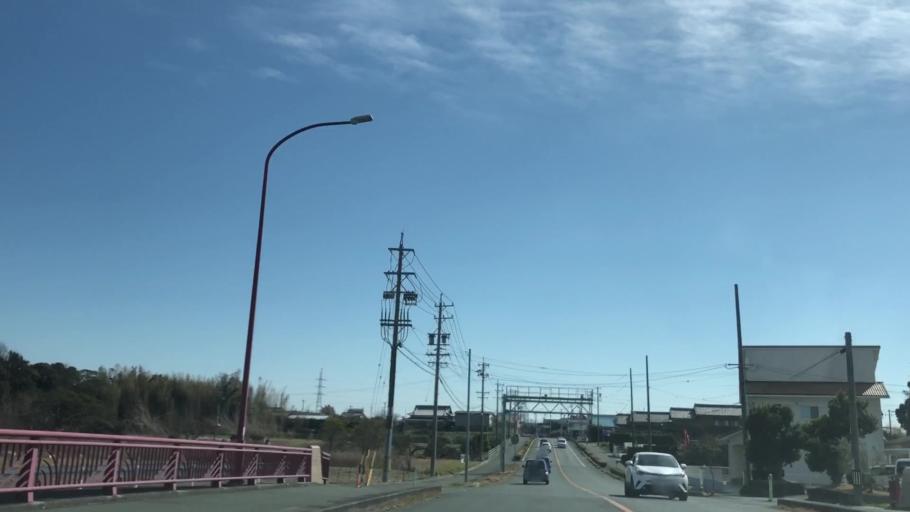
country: JP
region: Aichi
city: Toyohashi
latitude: 34.7153
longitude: 137.4063
